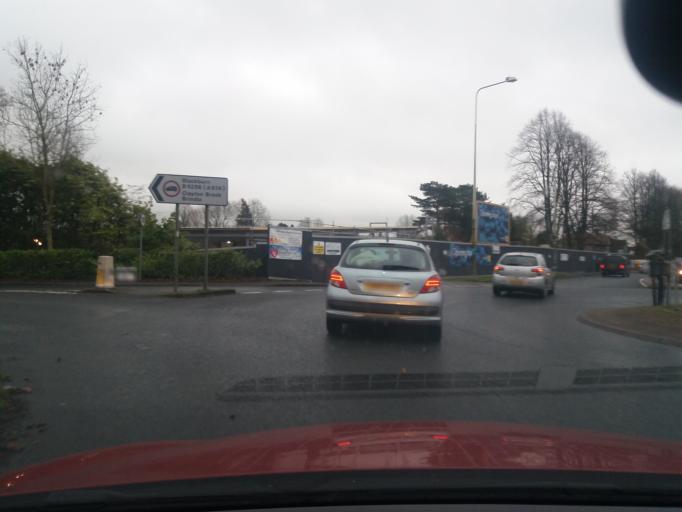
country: GB
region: England
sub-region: Lancashire
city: Clayton-le-Woods
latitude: 53.7070
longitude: -2.6395
